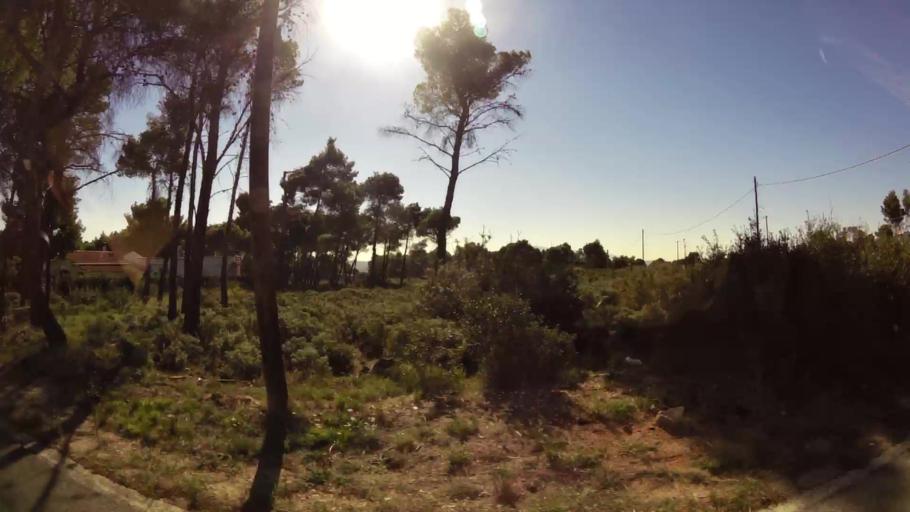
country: GR
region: Attica
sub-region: Nomarchia Anatolikis Attikis
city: Thrakomakedones
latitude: 38.1313
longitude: 23.7700
